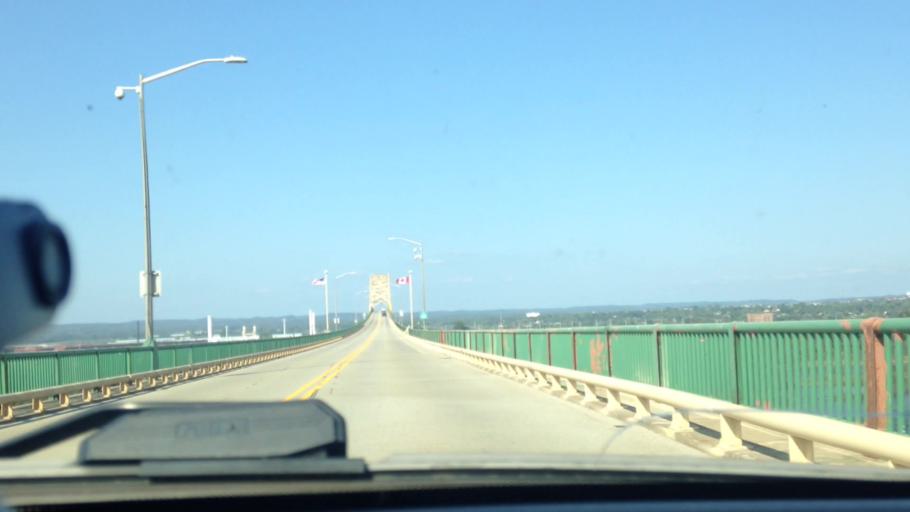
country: US
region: Michigan
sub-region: Chippewa County
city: Sault Ste. Marie
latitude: 46.5074
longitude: -84.3611
